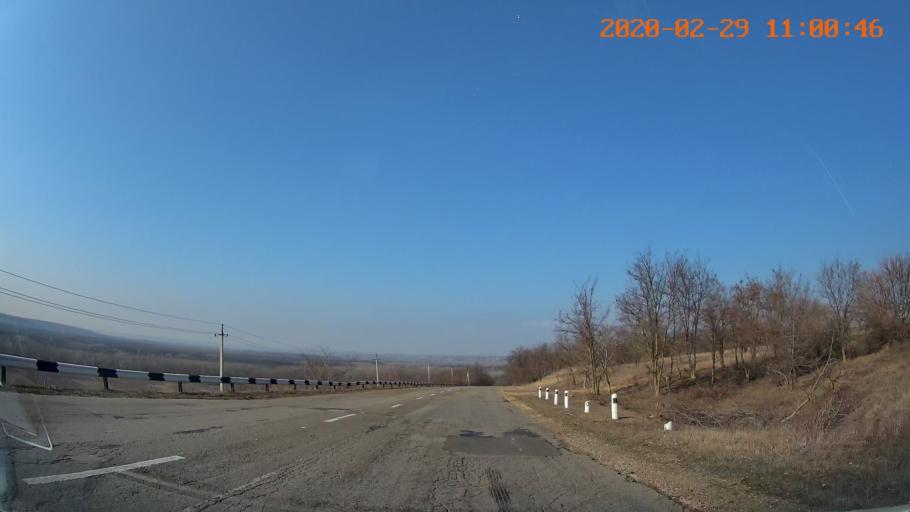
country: MD
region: Telenesti
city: Grigoriopol
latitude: 47.1606
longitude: 29.2711
